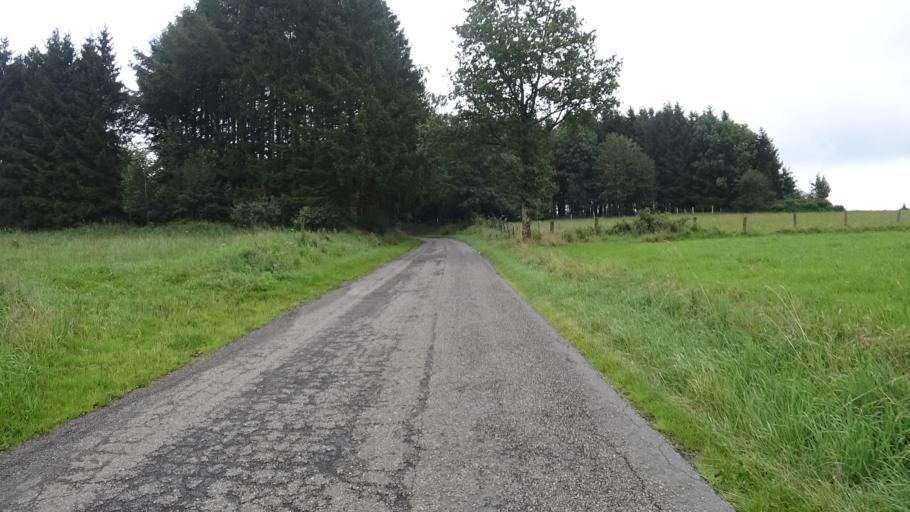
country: BE
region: Wallonia
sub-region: Province du Luxembourg
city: Chiny
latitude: 49.8091
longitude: 5.3356
